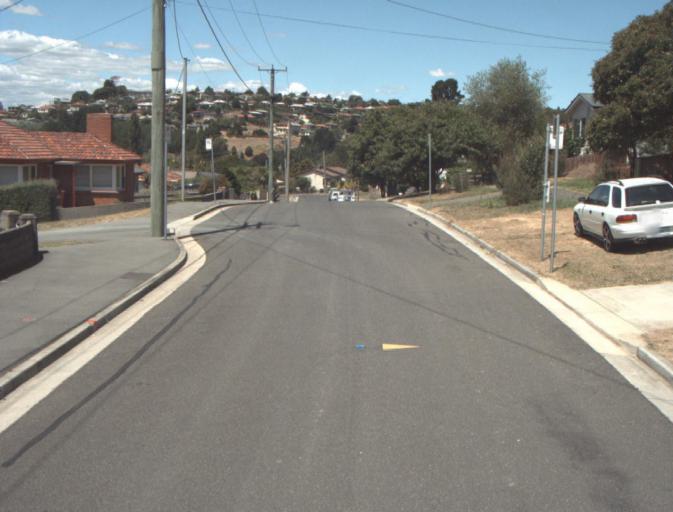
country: AU
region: Tasmania
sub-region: Launceston
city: West Launceston
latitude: -41.4564
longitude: 147.1382
